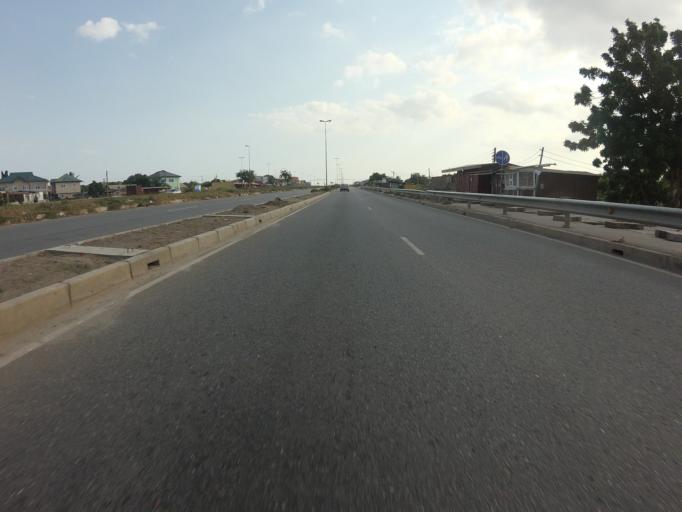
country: GH
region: Greater Accra
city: Achiaman
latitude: 5.6497
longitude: -0.3076
